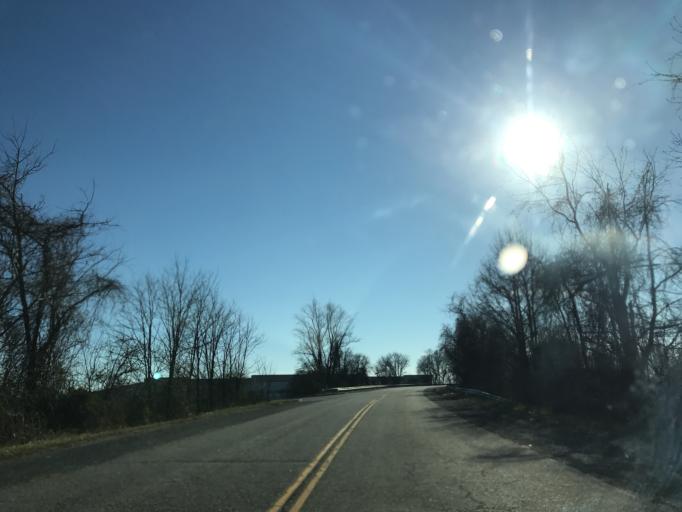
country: US
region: Maryland
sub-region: Harford County
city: Perryman
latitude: 39.4634
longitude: -76.1998
